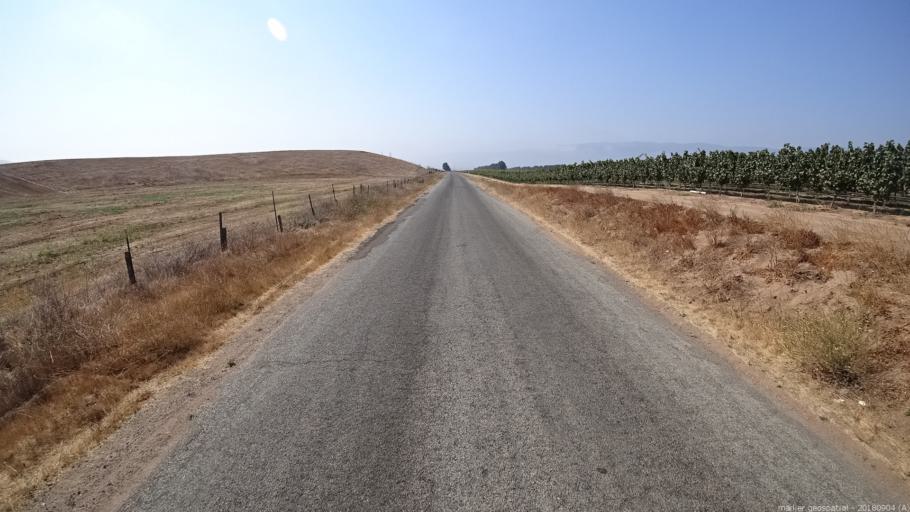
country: US
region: California
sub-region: Monterey County
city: Soledad
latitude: 36.4873
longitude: -121.3566
